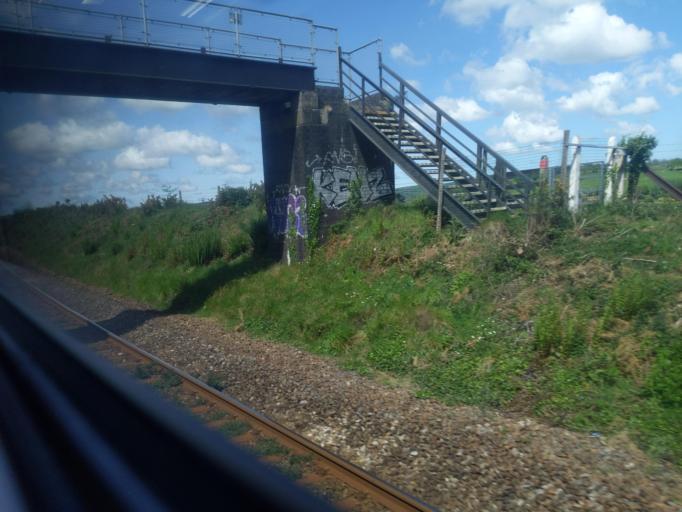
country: GB
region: England
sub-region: Cornwall
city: Liskeard
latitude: 50.4500
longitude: -4.4901
